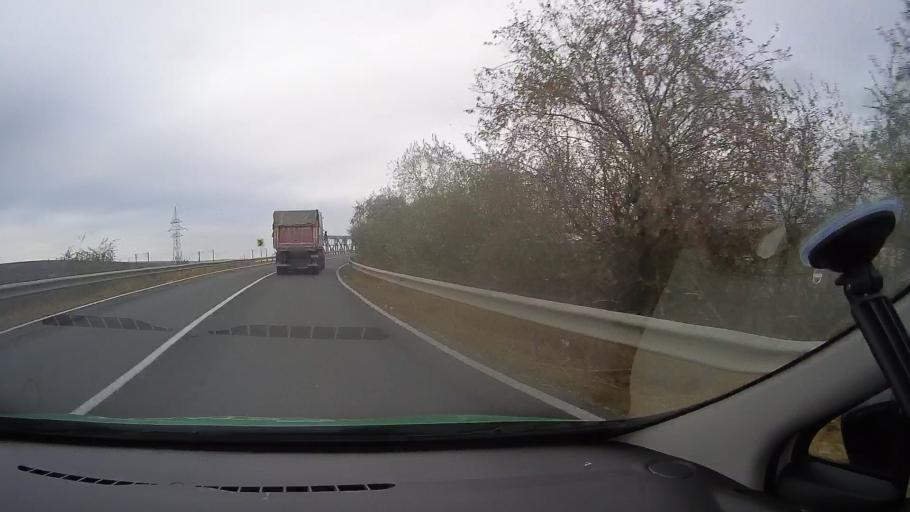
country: RO
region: Constanta
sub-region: Comuna Poarta Alba
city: Poarta Alba
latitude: 44.2152
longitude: 28.3906
